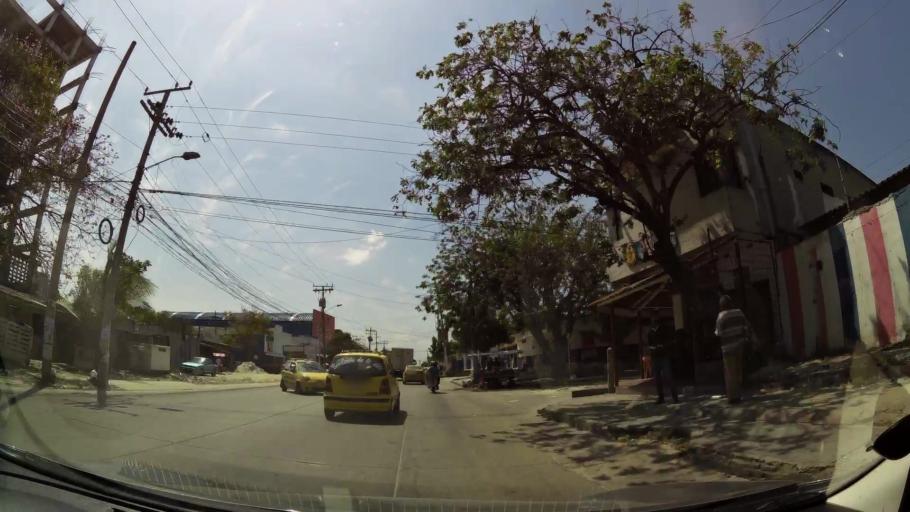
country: CO
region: Atlantico
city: Barranquilla
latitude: 10.9567
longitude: -74.8058
